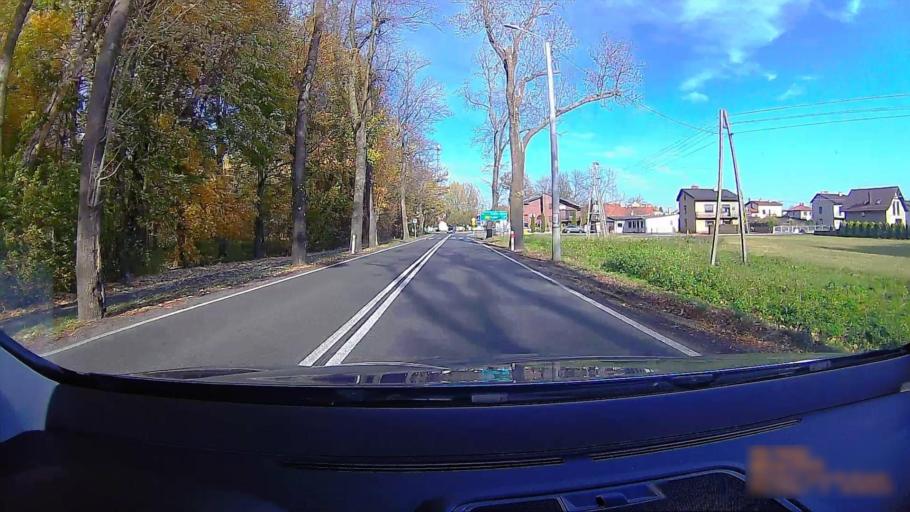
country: PL
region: Greater Poland Voivodeship
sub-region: Powiat ostrzeszowski
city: Doruchow
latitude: 51.4152
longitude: 18.0759
